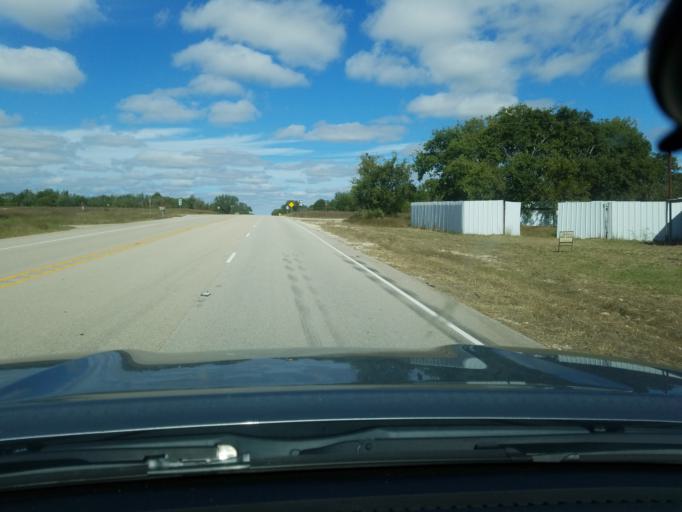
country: US
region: Texas
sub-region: Hamilton County
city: Hamilton
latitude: 31.5919
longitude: -98.1568
